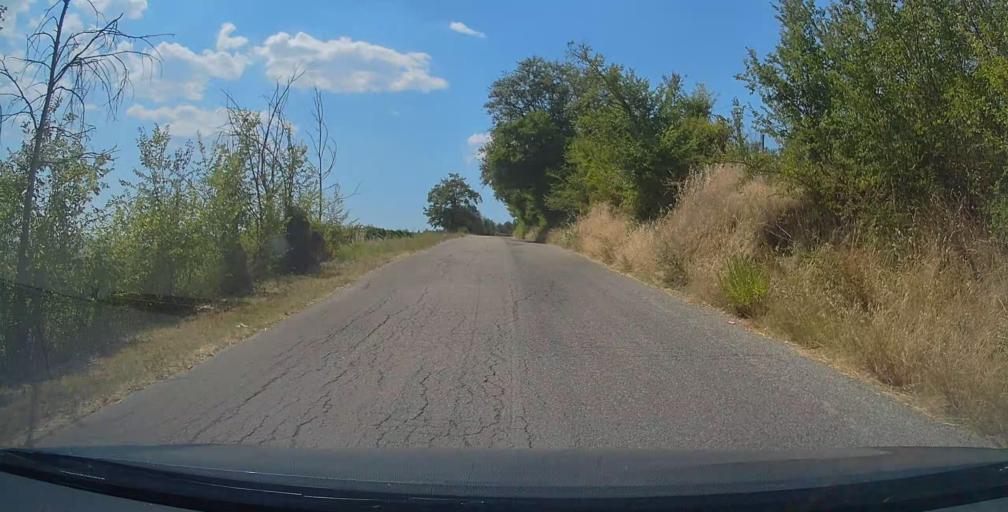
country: IT
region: Umbria
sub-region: Provincia di Terni
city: Otricoli
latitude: 42.4008
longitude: 12.4928
